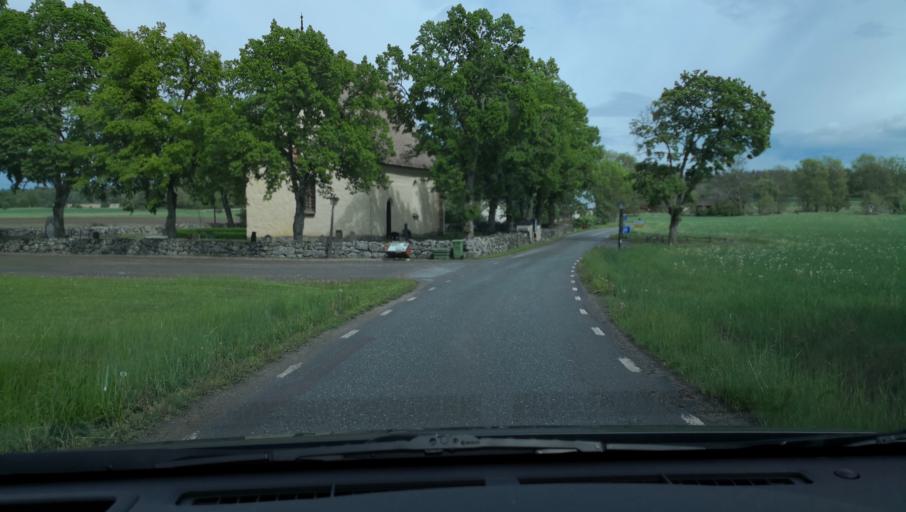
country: SE
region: Uppsala
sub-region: Enkopings Kommun
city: Orsundsbro
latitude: 59.7207
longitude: 17.4284
